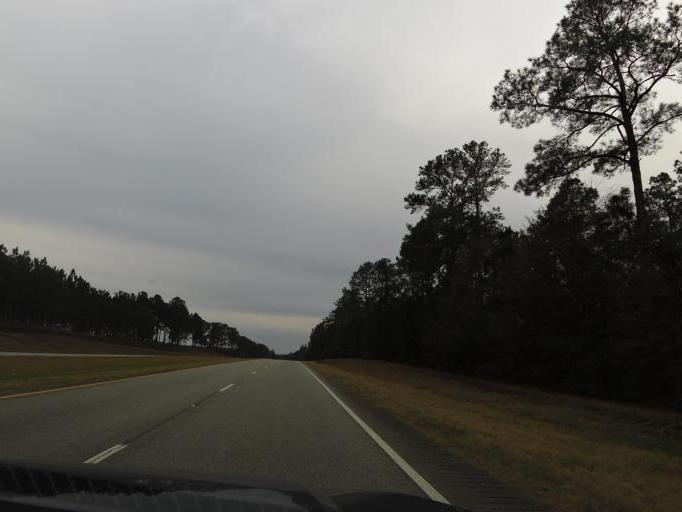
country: US
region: Georgia
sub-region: Thomas County
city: Boston
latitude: 30.6895
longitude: -83.8872
